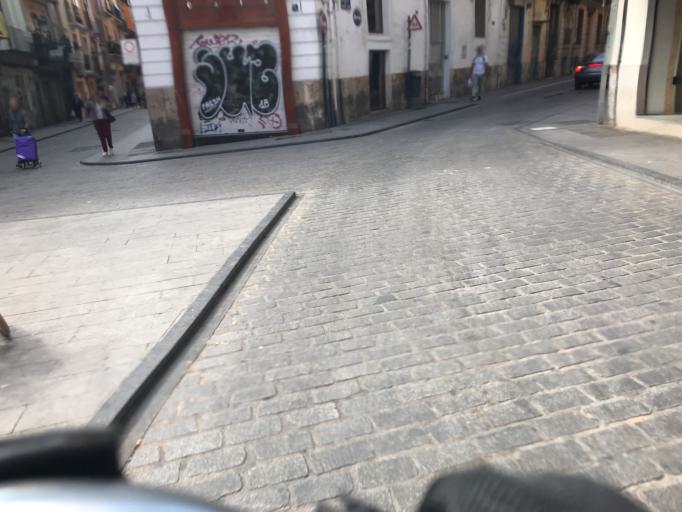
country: ES
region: Valencia
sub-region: Provincia de Valencia
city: Valencia
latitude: 39.4762
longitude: -0.3804
